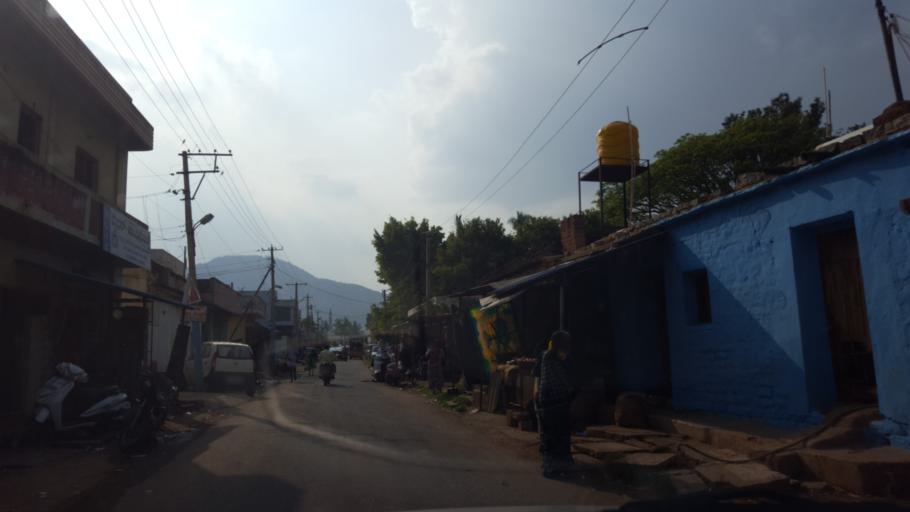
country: IN
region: Karnataka
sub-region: Chikkaballapur
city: Chik Ballapur
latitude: 13.3861
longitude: 77.6995
